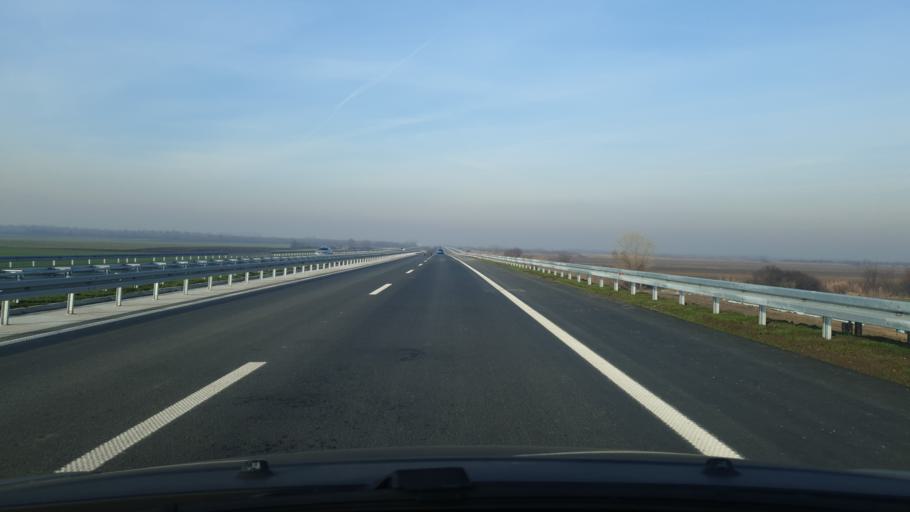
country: RS
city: Umka
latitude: 44.6935
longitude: 20.2669
